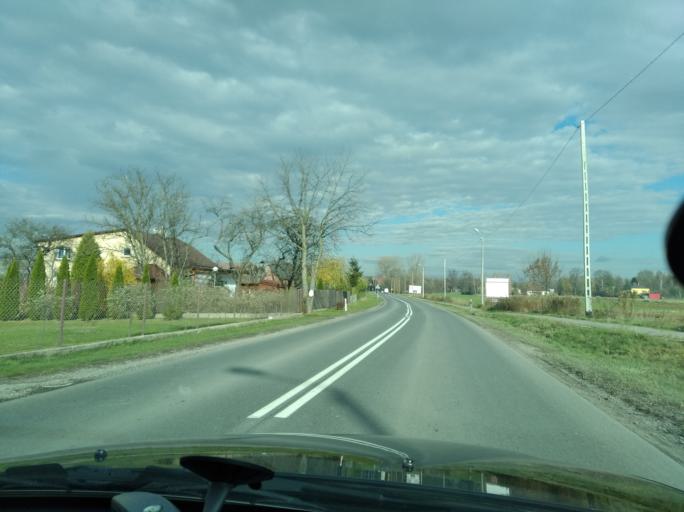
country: PL
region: Subcarpathian Voivodeship
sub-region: Powiat ropczycko-sedziszowski
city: Ostrow
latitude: 50.0919
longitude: 21.5925
